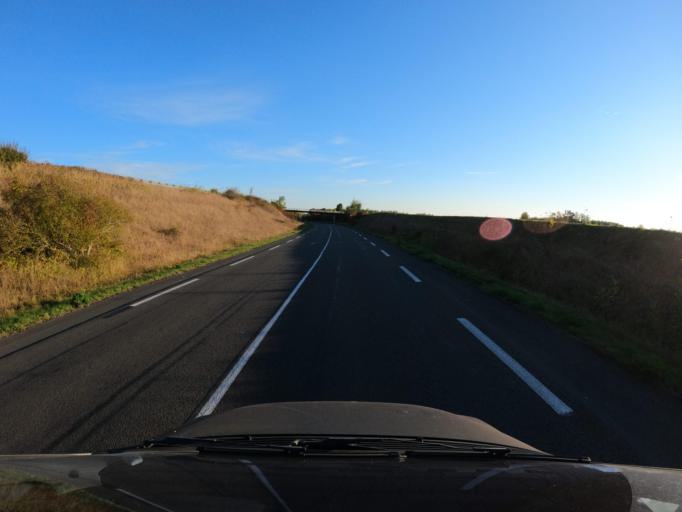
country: FR
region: Pays de la Loire
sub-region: Departement de la Vendee
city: Sainte-Hermine
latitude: 46.5609
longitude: -1.0467
